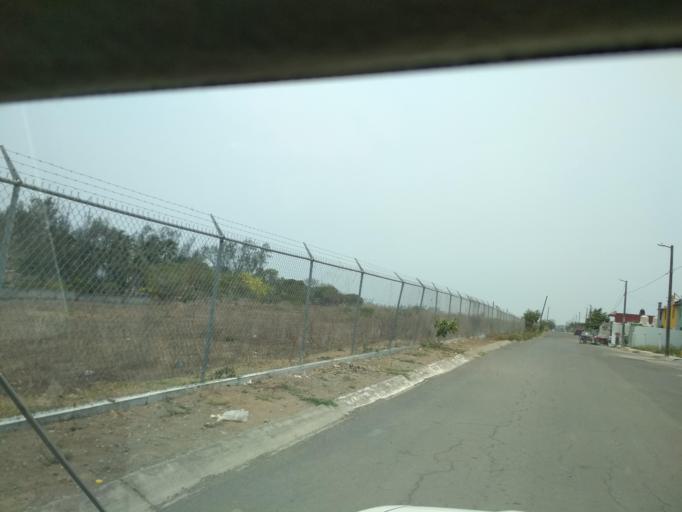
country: MX
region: Veracruz
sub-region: Veracruz
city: Las Amapolas
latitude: 19.1553
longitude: -96.2133
